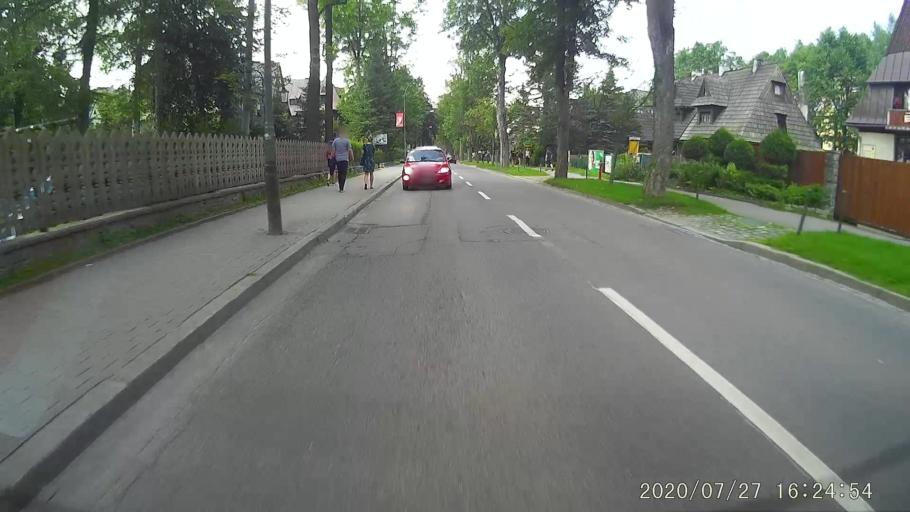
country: PL
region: Lesser Poland Voivodeship
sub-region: Powiat tatrzanski
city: Zakopane
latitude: 49.2970
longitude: 19.9632
